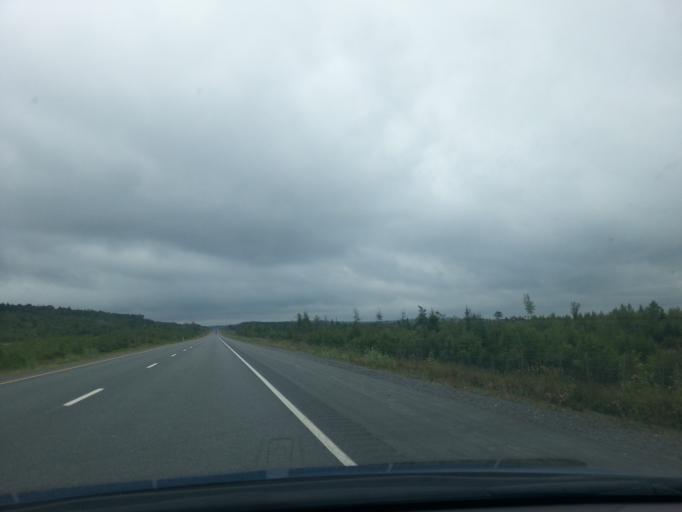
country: CA
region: New Brunswick
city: Nackawic
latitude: 45.9214
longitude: -67.1520
